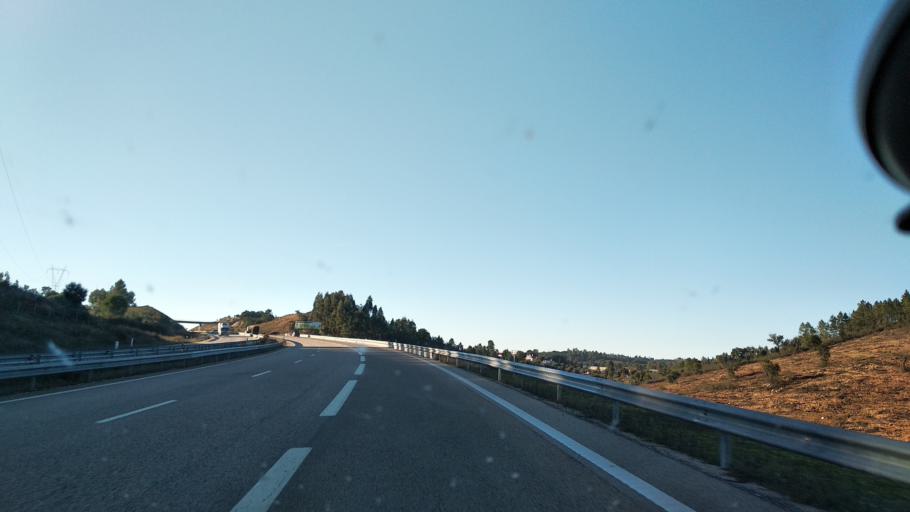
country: PT
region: Santarem
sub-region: Abrantes
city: Alferrarede
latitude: 39.4951
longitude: -8.0741
